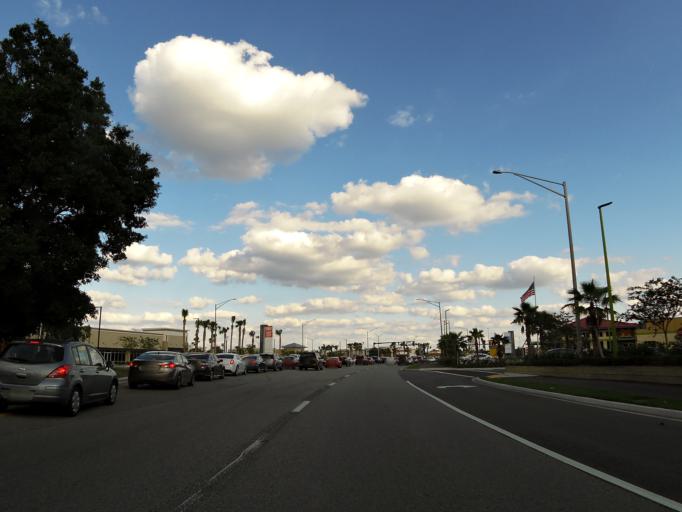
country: US
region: Florida
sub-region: Duval County
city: Jacksonville
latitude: 30.2561
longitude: -81.5377
